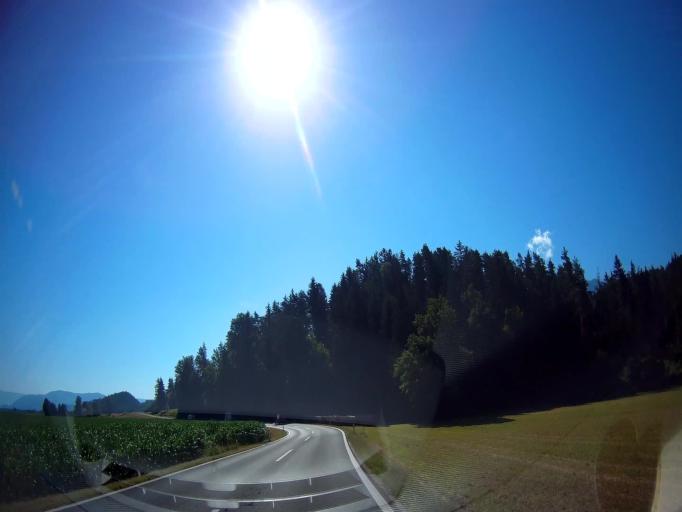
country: AT
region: Carinthia
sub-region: Politischer Bezirk Volkermarkt
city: Globasnitz
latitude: 46.5676
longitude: 14.6839
